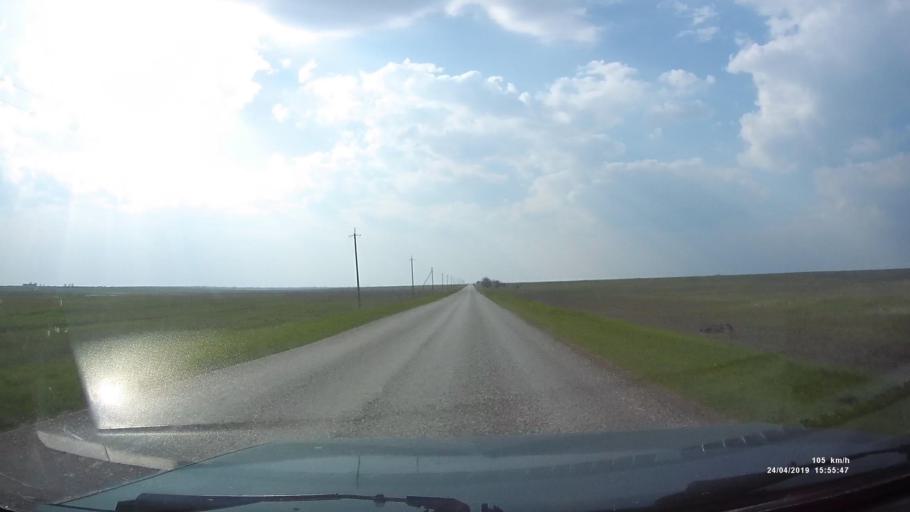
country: RU
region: Kalmykiya
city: Yashalta
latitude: 46.5929
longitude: 42.5422
